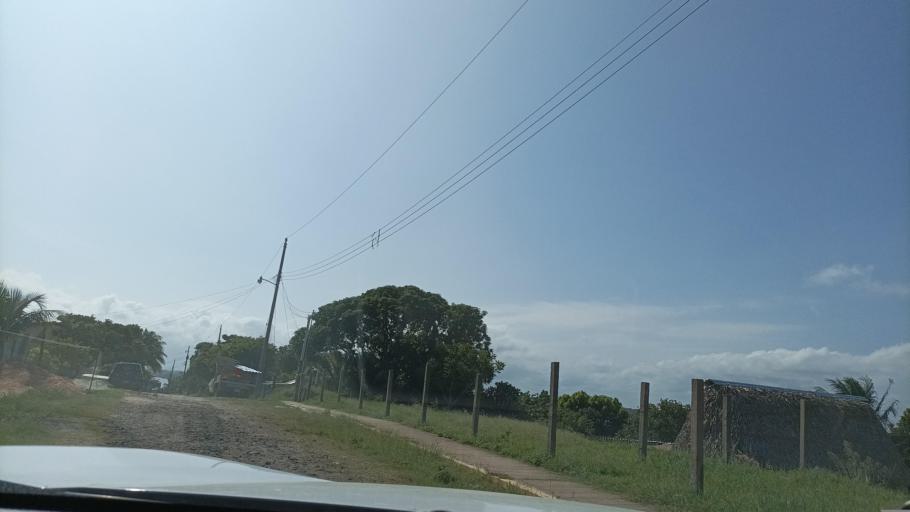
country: MX
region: Veracruz
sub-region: Coatzacoalcos
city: Fraccionamiento Ciudad Olmeca
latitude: 18.2146
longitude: -94.6146
